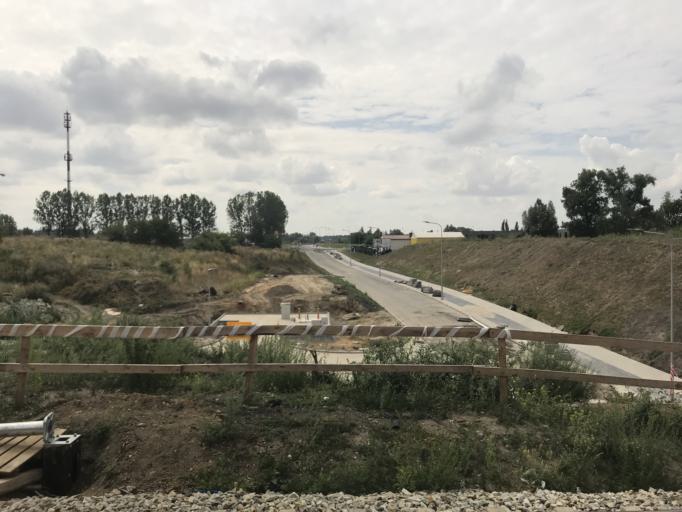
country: PL
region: Greater Poland Voivodeship
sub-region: Powiat gnieznienski
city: Gniezno
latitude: 52.5312
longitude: 17.6218
